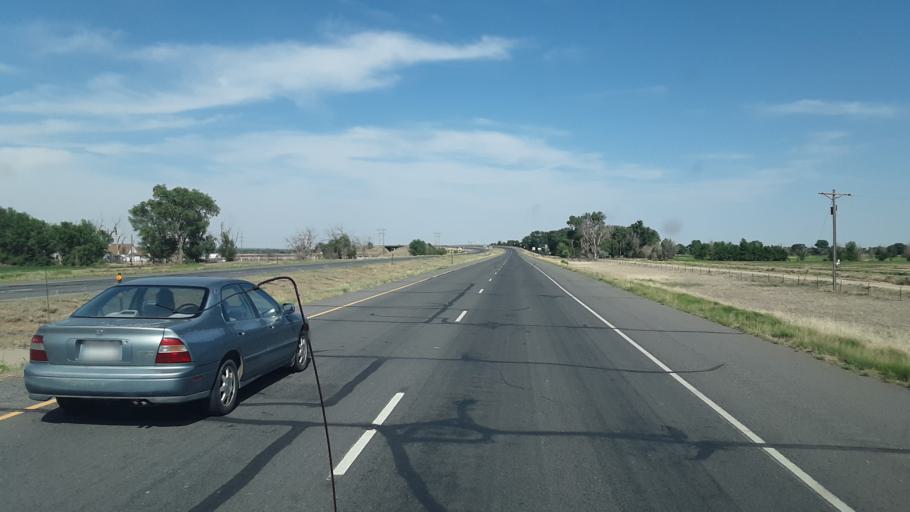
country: US
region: Colorado
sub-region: Otero County
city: Rocky Ford
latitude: 38.1034
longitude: -103.8525
